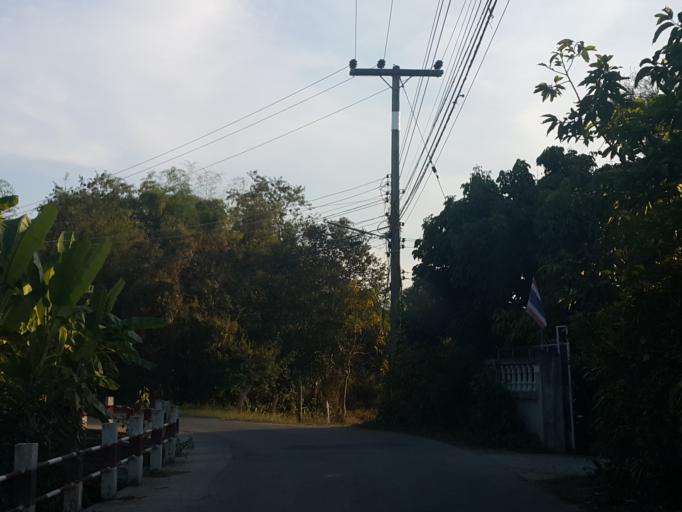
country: TH
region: Chiang Mai
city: San Sai
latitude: 18.8179
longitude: 99.0977
